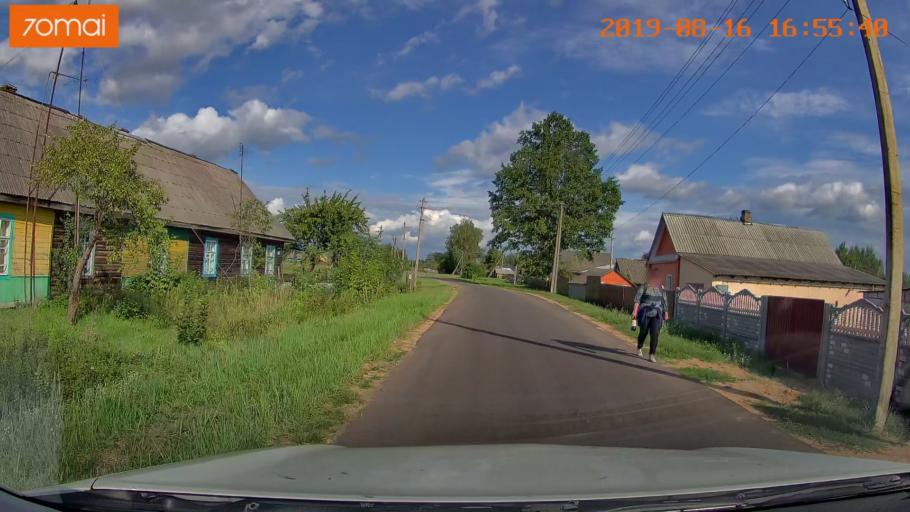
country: BY
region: Mogilev
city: Hlusha
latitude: 53.2536
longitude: 28.8137
